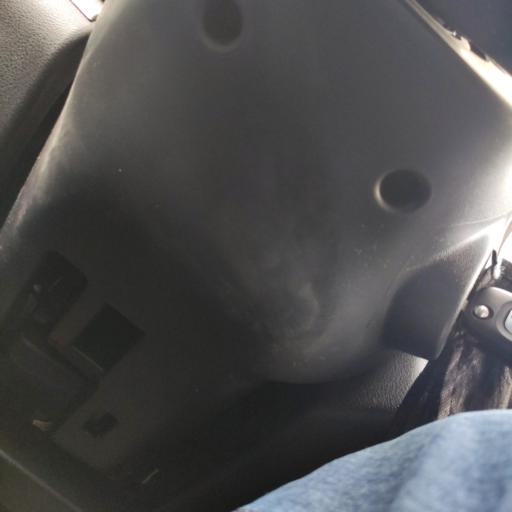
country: RU
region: Samara
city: Smyshlyayevka
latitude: 53.2188
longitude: 50.3338
